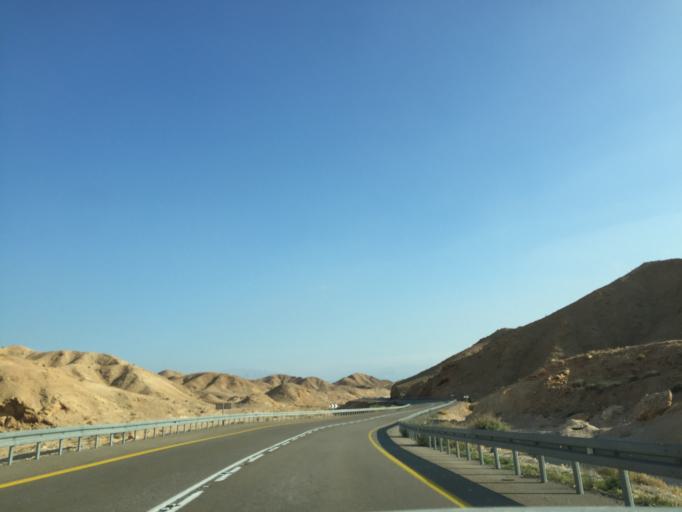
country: IL
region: Southern District
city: `En Boqeq
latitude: 31.1898
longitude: 35.2848
